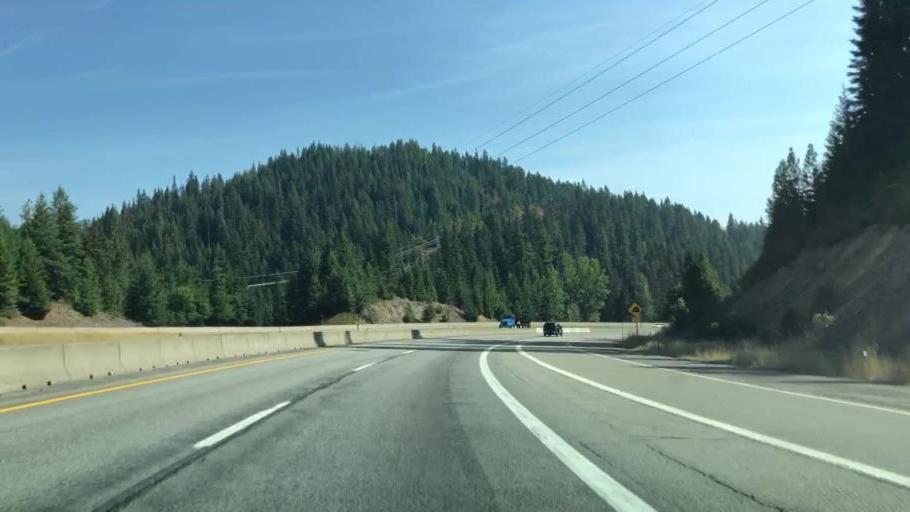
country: US
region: Idaho
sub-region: Kootenai County
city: Coeur d'Alene
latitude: 47.6199
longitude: -116.5210
